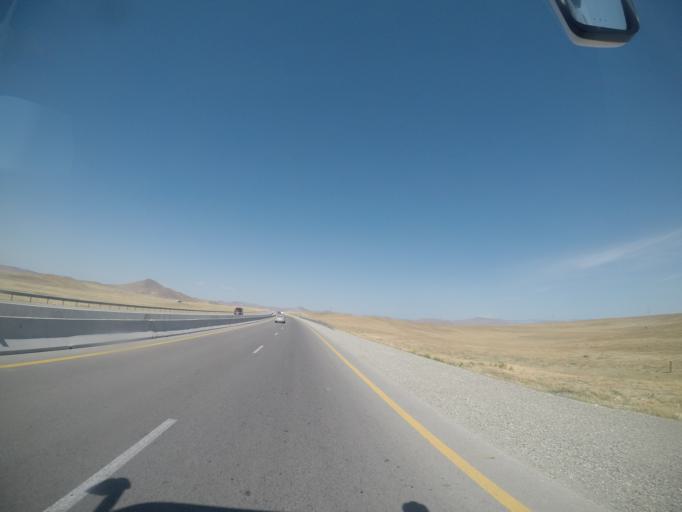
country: AZ
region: Sumqayit
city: Haci Zeynalabdin
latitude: 40.4859
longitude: 49.4262
